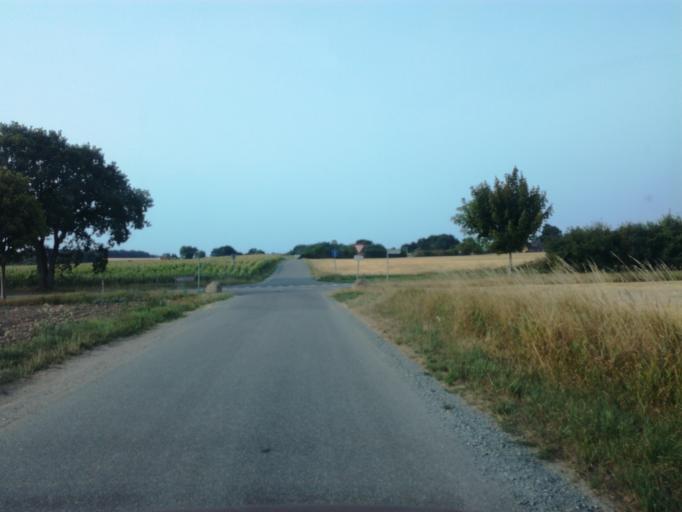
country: DK
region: South Denmark
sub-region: Vejle Kommune
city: Borkop
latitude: 55.6379
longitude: 9.6139
